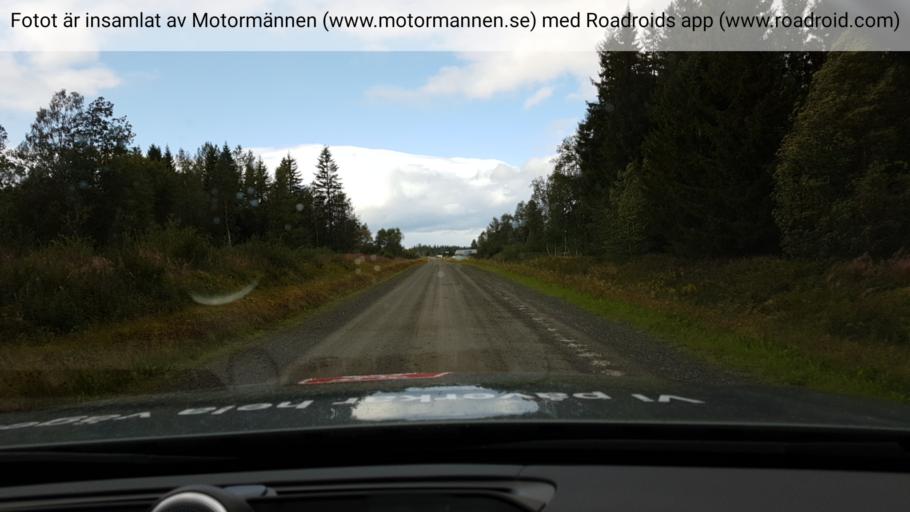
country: SE
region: Jaemtland
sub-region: OEstersunds Kommun
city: Lit
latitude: 63.6787
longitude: 14.8645
